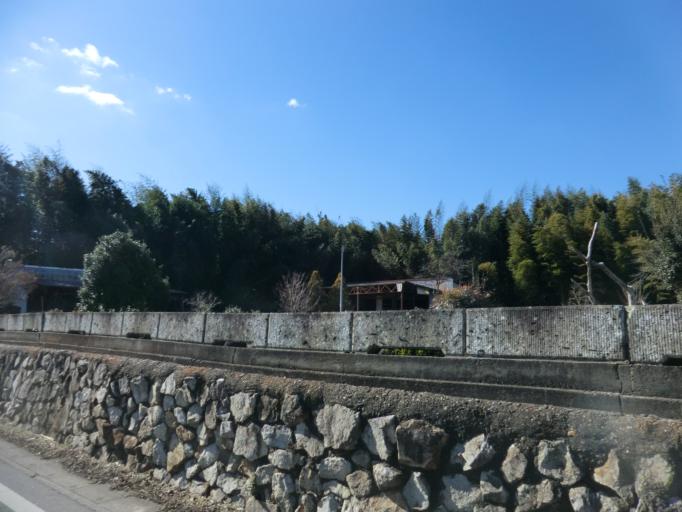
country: JP
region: Ibaraki
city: Ishige
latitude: 36.1682
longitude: 140.0169
